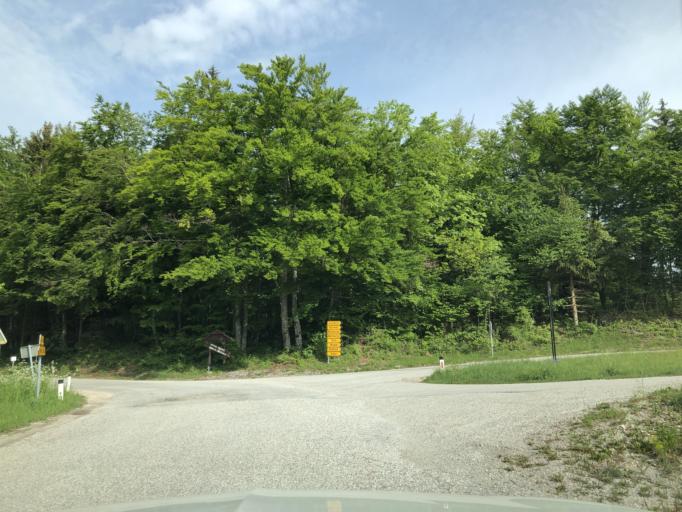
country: SI
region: Bloke
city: Nova Vas
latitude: 45.8017
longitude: 14.5509
